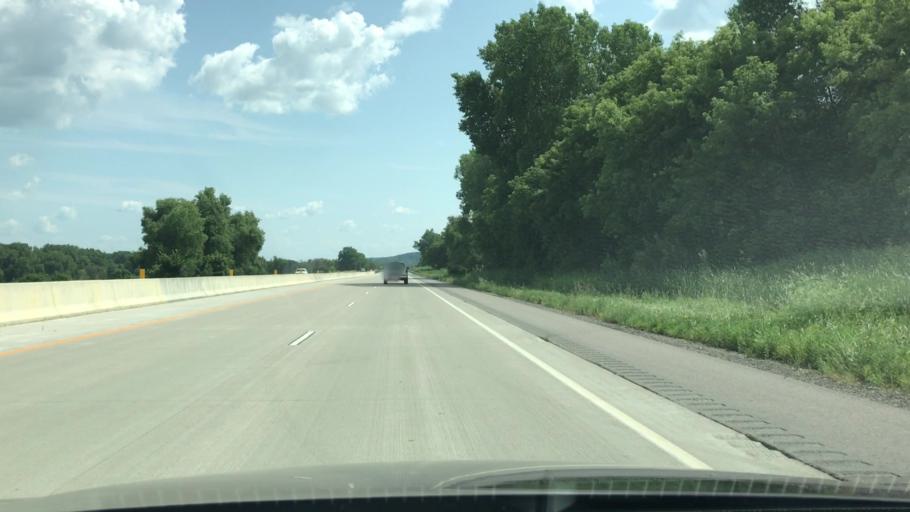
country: US
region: Minnesota
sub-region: Nicollet County
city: North Mankato
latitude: 44.2465
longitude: -94.0275
